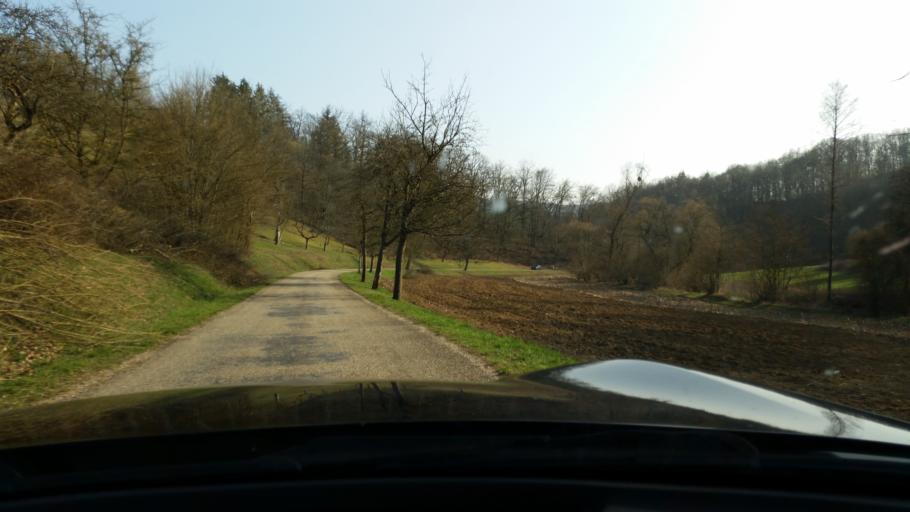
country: DE
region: Baden-Wuerttemberg
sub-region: Regierungsbezirk Stuttgart
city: Mockmuhl
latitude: 49.3233
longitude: 9.3894
